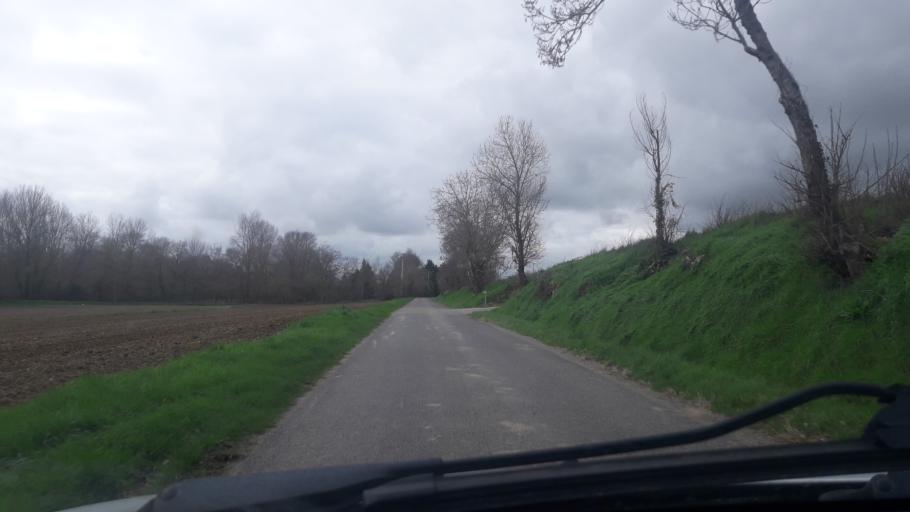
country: FR
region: Midi-Pyrenees
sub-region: Departement du Gers
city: Pujaudran
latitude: 43.6221
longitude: 1.0697
